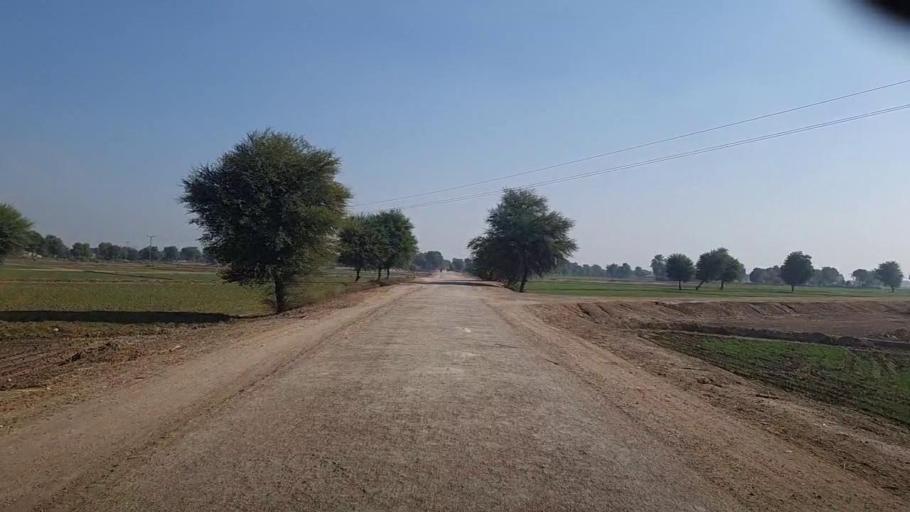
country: PK
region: Sindh
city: Darya Khan Marri
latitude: 26.6662
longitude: 68.3360
